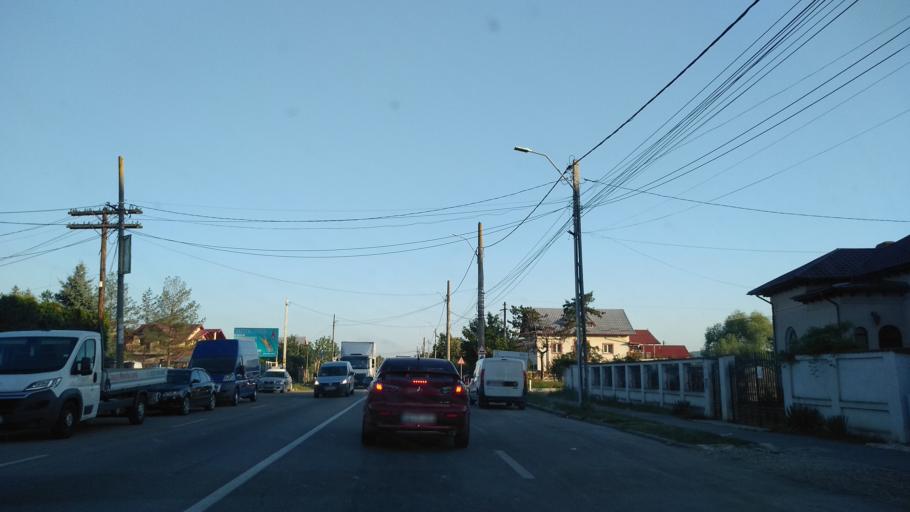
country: RO
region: Arges
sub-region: Comuna Bascov
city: Bascov
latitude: 44.8929
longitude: 24.8206
